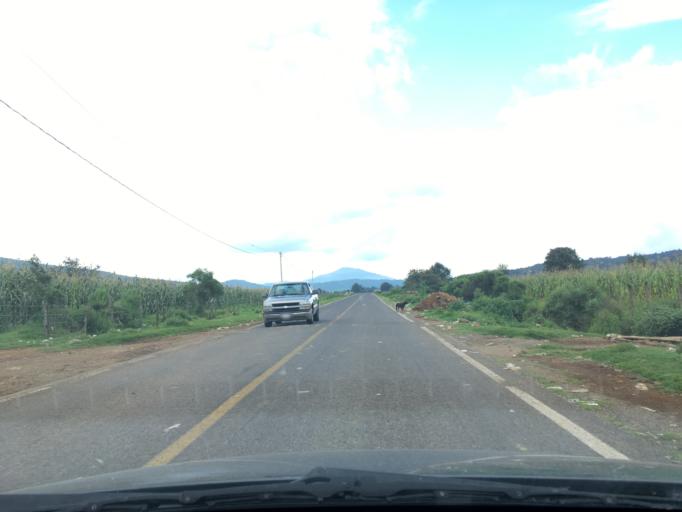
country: MX
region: Michoacan
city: Pichataro
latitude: 19.5681
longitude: -101.8101
